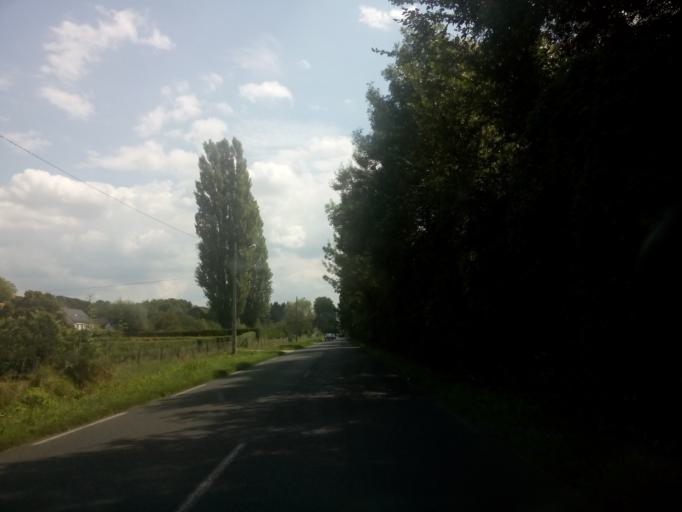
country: FR
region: Centre
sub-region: Departement d'Indre-et-Loire
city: Cheille
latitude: 47.2701
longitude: 0.4293
